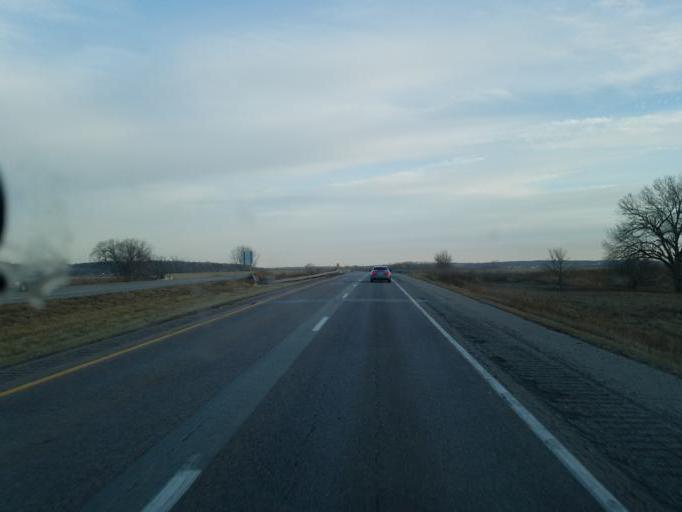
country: US
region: Iowa
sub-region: Harrison County
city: Missouri Valley
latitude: 41.5747
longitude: -95.9295
